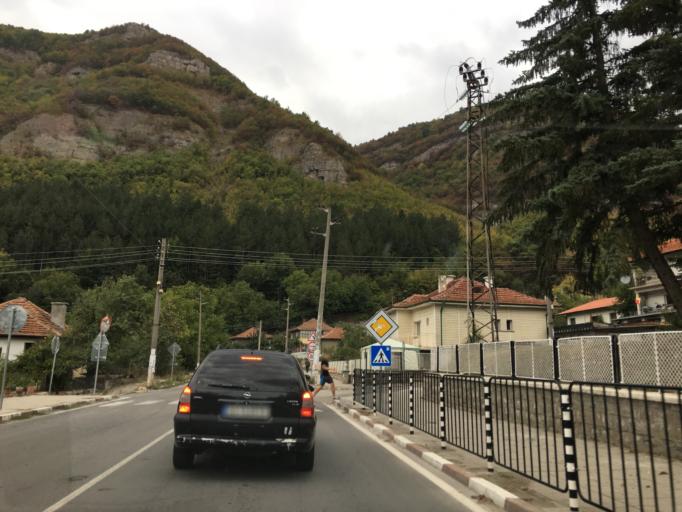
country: BG
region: Sofiya
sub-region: Obshtina Svoge
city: Svoge
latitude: 43.0030
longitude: 23.3460
